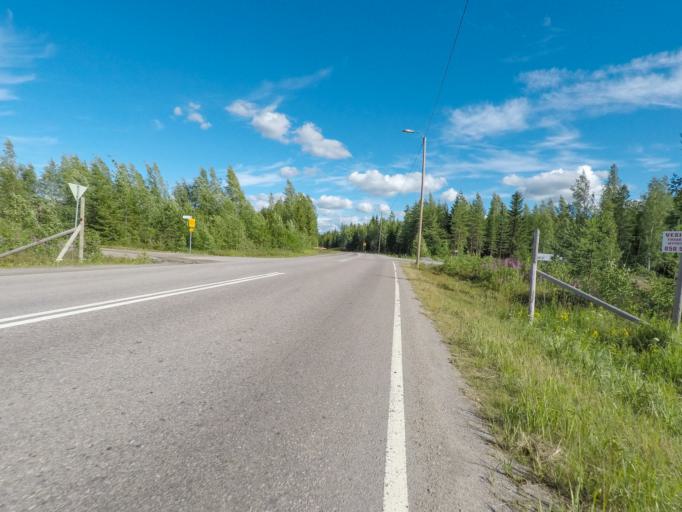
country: FI
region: South Karelia
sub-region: Lappeenranta
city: Joutseno
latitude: 61.1478
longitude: 28.6173
